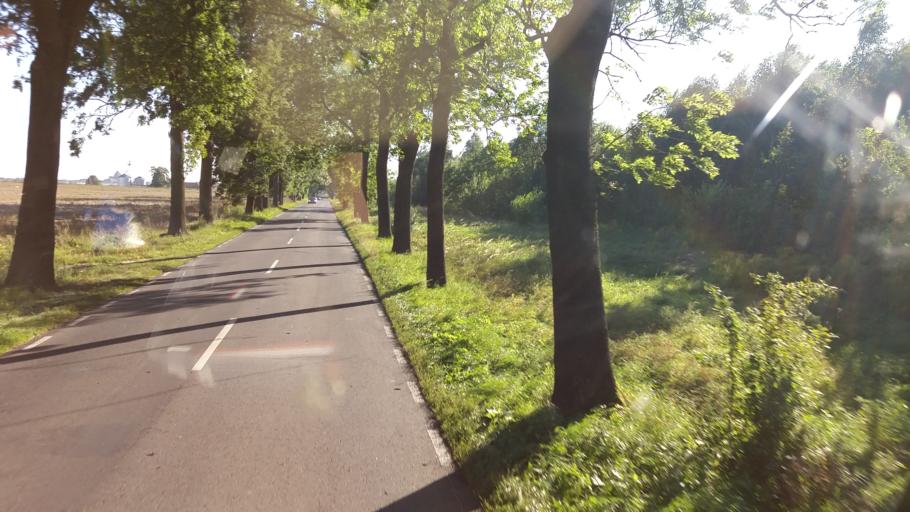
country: PL
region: West Pomeranian Voivodeship
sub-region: Powiat choszczenski
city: Choszczno
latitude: 53.1884
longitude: 15.4321
